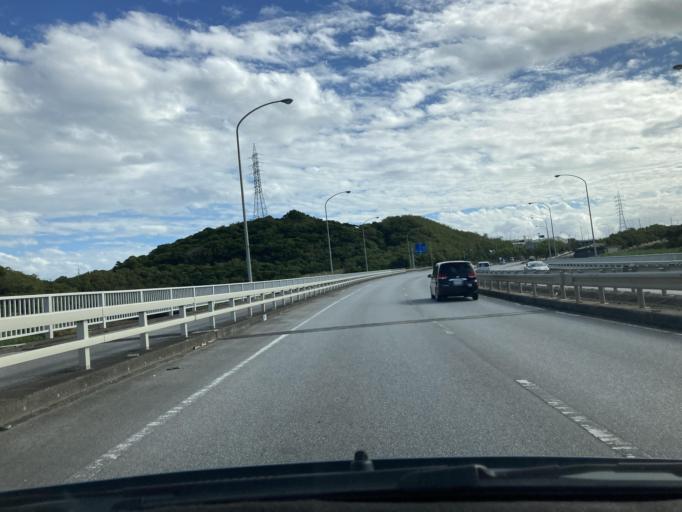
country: JP
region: Okinawa
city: Tomigusuku
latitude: 26.1773
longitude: 127.7270
